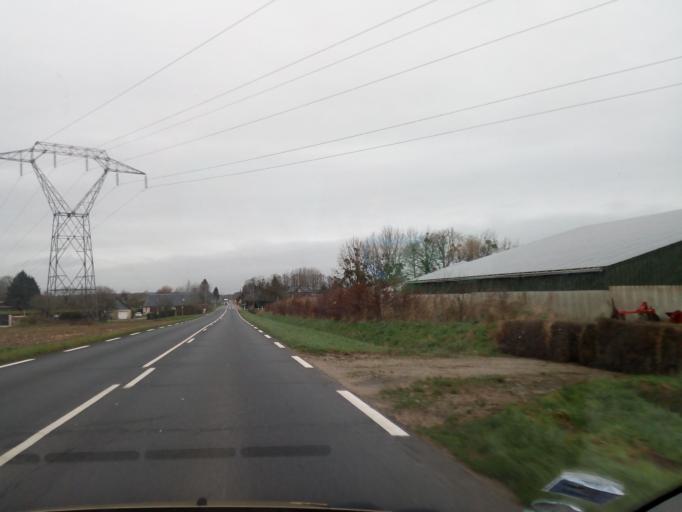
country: FR
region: Haute-Normandie
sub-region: Departement de l'Eure
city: Hauville
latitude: 49.3987
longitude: 0.7978
